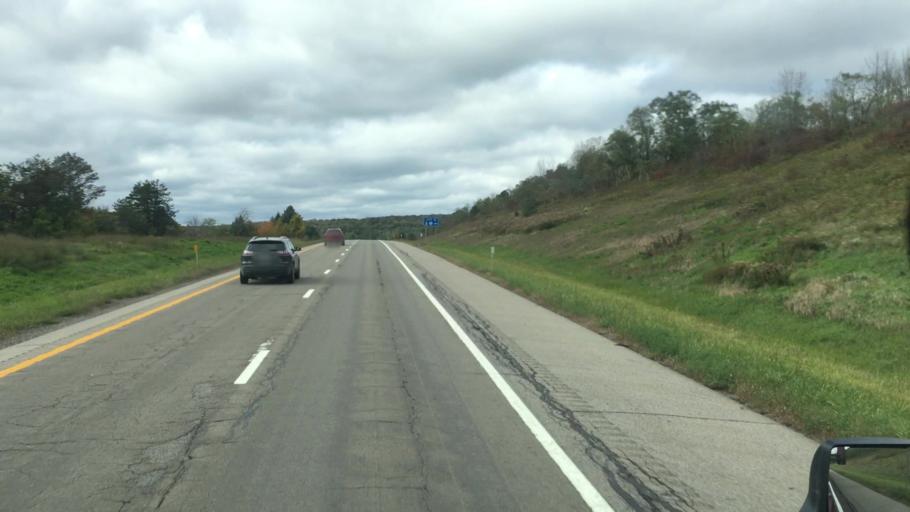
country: US
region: New York
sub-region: Chautauqua County
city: Celoron
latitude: 42.1218
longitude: -79.2611
